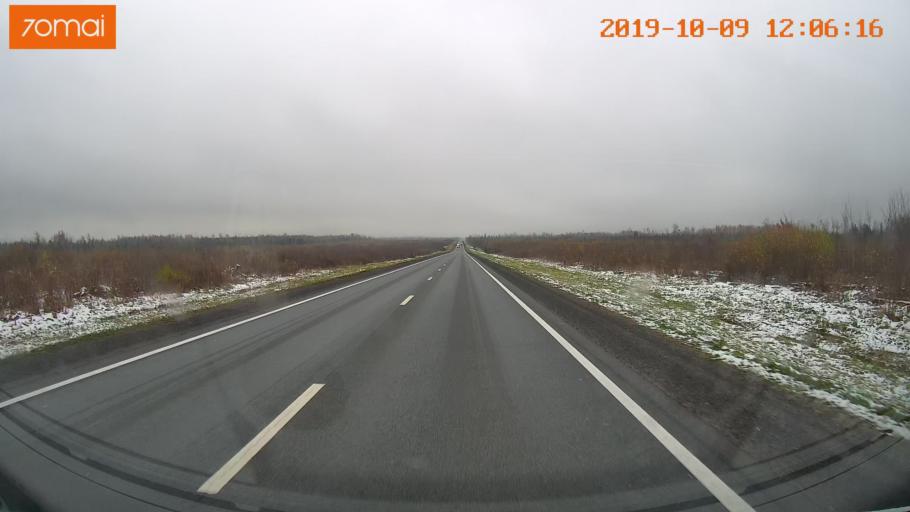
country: RU
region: Jaroslavl
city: Prechistoye
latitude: 58.6171
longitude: 40.3340
